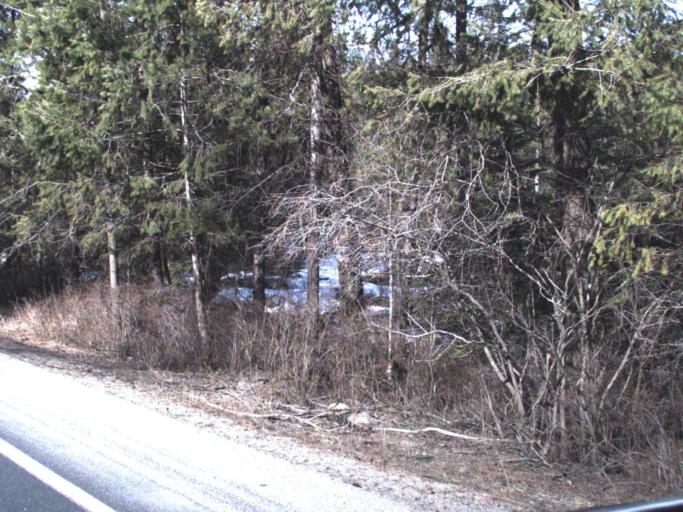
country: US
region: Washington
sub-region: Stevens County
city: Colville
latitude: 48.5089
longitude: -117.7035
